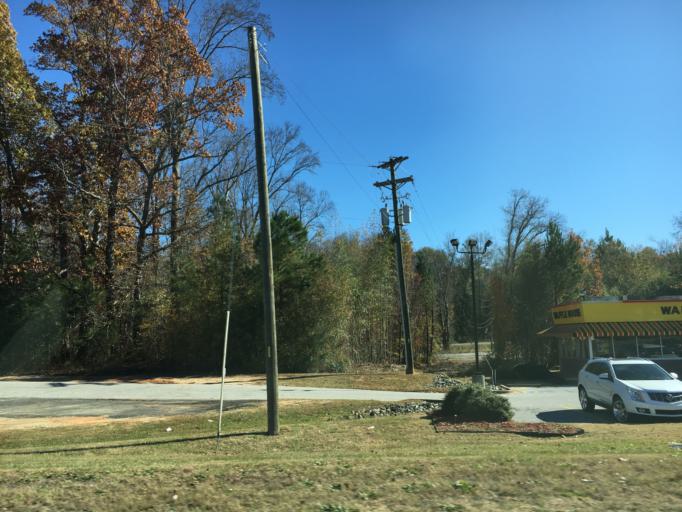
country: US
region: South Carolina
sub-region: Spartanburg County
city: Roebuck
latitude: 34.8393
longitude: -81.9695
